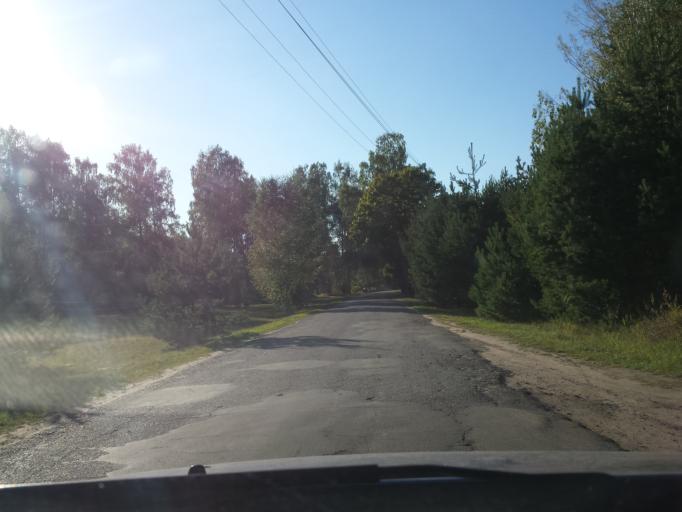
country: LV
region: Carnikava
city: Carnikava
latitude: 57.1148
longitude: 24.2414
